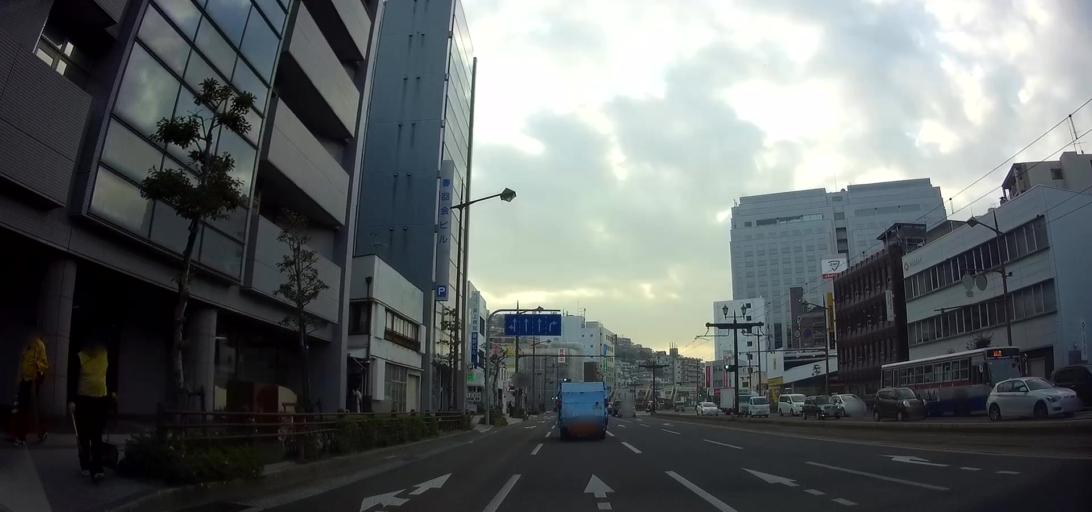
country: JP
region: Nagasaki
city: Nagasaki-shi
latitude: 32.7592
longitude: 129.8670
